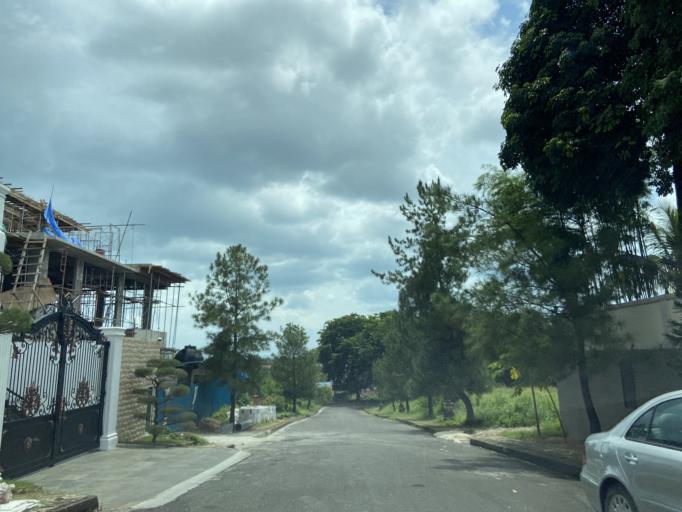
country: SG
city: Singapore
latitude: 1.1297
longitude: 103.9975
